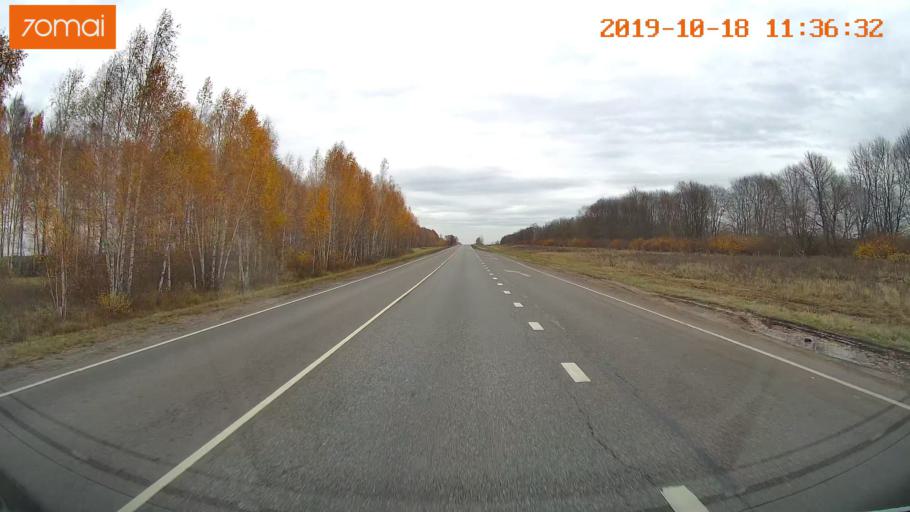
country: RU
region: Rjazan
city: Oktyabr'skiy
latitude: 54.1418
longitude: 38.8089
